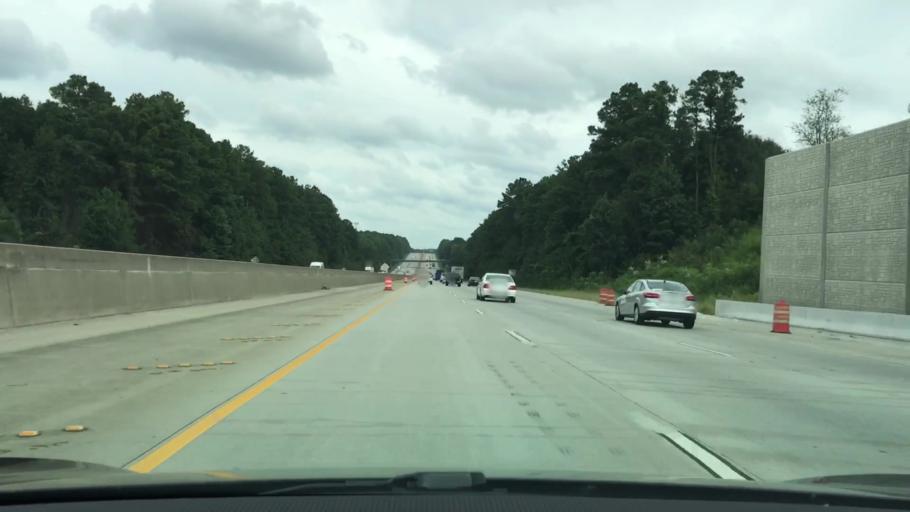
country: US
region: Georgia
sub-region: Coweta County
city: East Newnan
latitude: 33.3676
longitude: -84.7593
